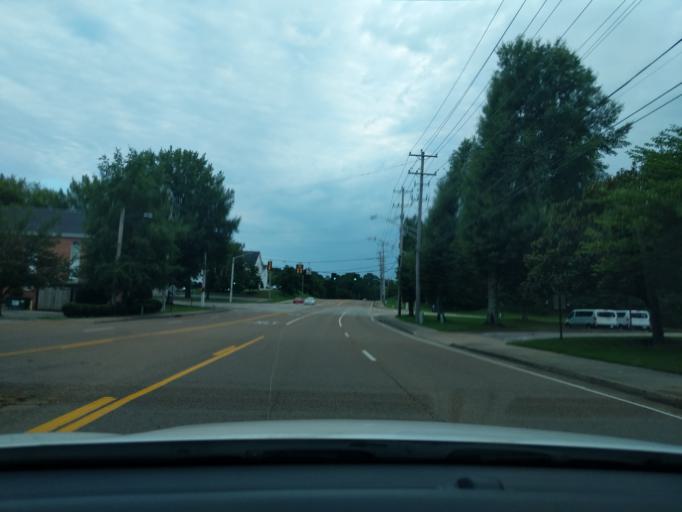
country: US
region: Tennessee
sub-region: Shelby County
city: Germantown
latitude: 35.0859
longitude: -89.8115
